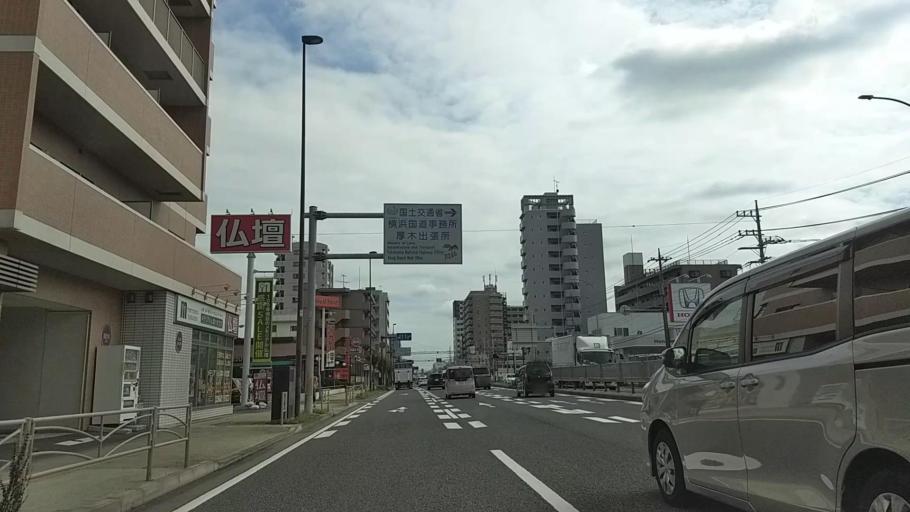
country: JP
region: Kanagawa
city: Atsugi
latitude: 35.4411
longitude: 139.3578
